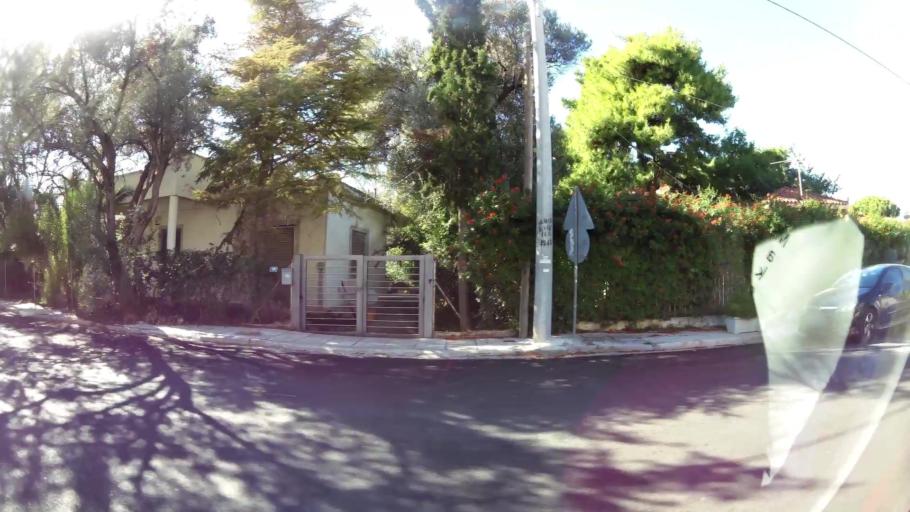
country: GR
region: Attica
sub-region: Nomarchia Anatolikis Attikis
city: Leondarion
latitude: 37.9854
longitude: 23.8547
